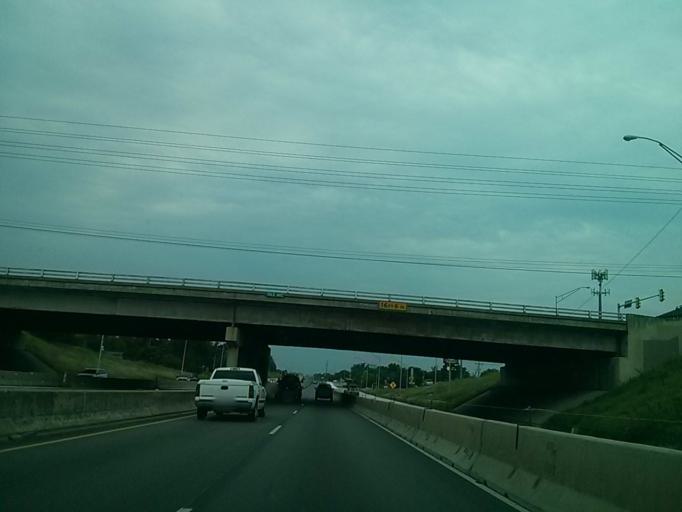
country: US
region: Oklahoma
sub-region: Tulsa County
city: Tulsa
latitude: 36.1593
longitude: -95.9216
